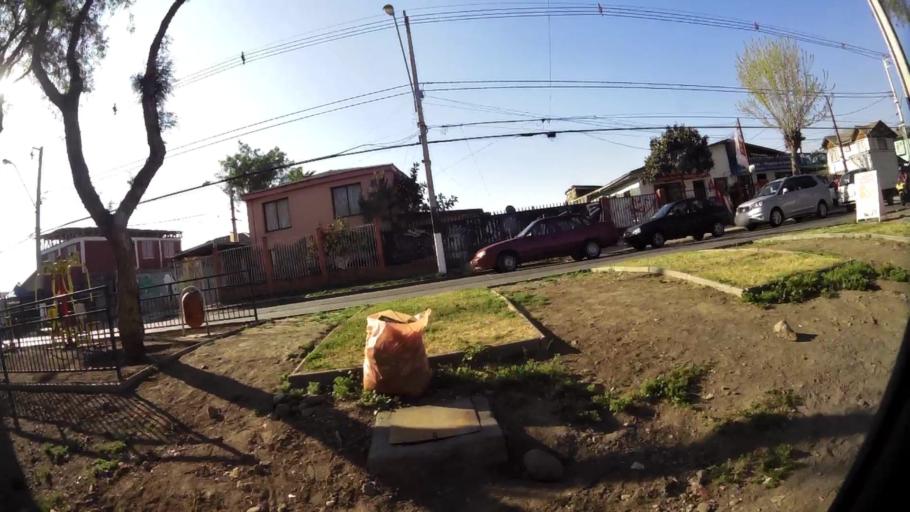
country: CL
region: Santiago Metropolitan
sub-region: Provincia de Santiago
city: Lo Prado
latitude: -33.4892
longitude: -70.7638
